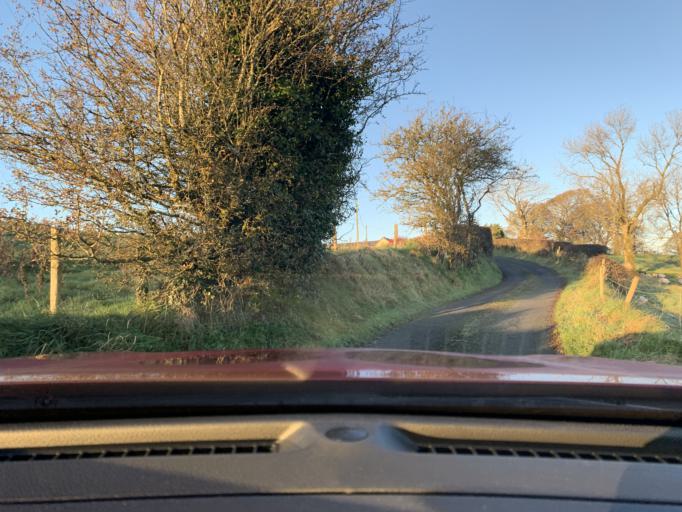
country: IE
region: Connaught
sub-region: Sligo
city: Ballymote
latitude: 54.0691
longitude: -8.5500
